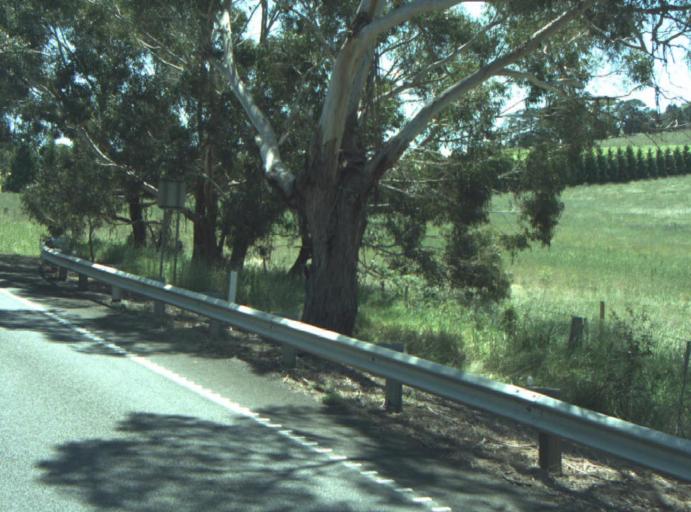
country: AU
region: Victoria
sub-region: Greater Geelong
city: Lara
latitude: -37.8870
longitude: 144.2574
